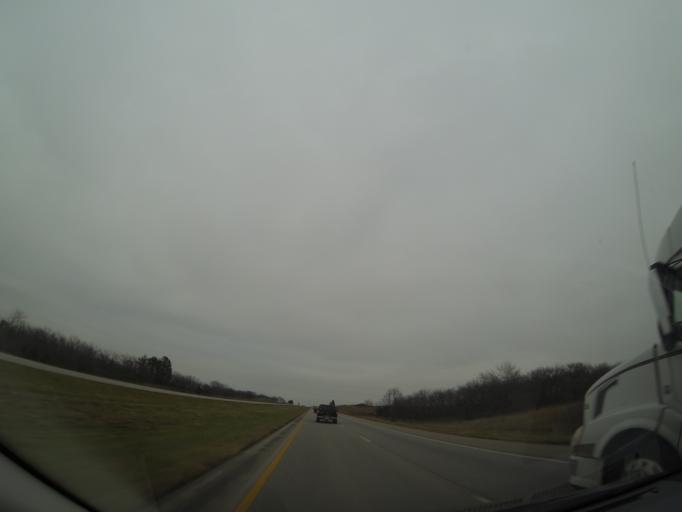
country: US
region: Nebraska
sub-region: Seward County
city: Milford
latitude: 40.8211
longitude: -96.9888
